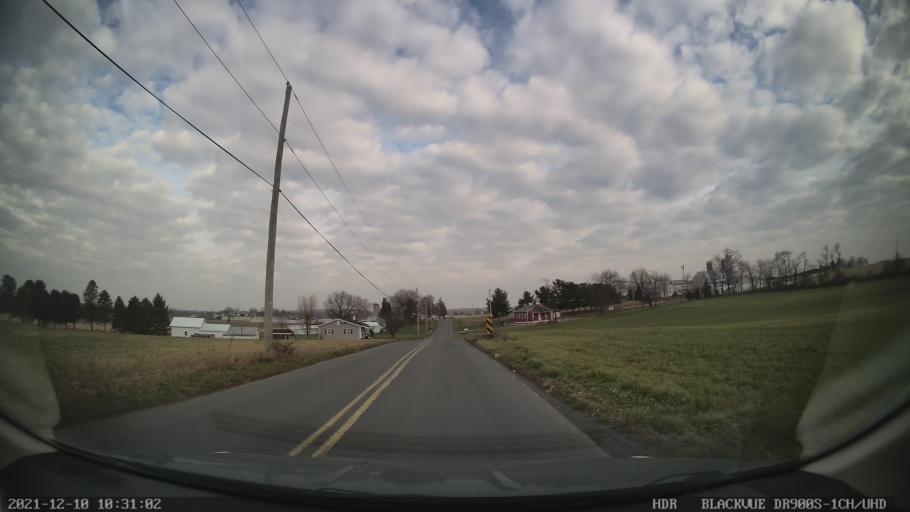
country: US
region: Pennsylvania
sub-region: Berks County
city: Topton
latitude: 40.5201
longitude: -75.7194
